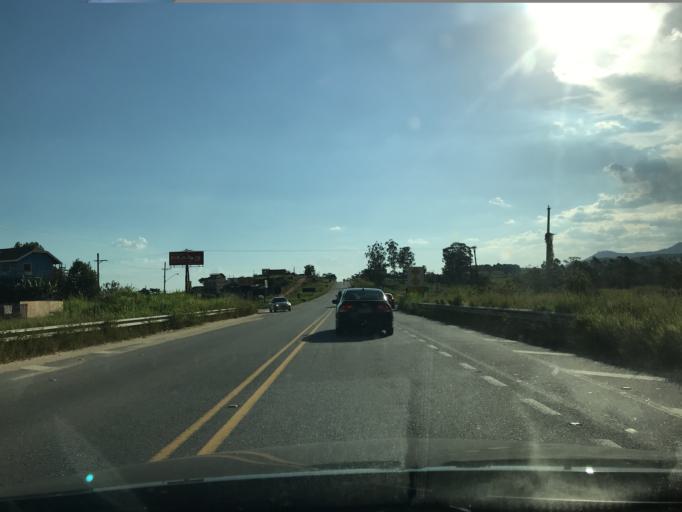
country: BR
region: Sao Paulo
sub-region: Tremembe
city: Tremembe
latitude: -22.9556
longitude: -45.6242
